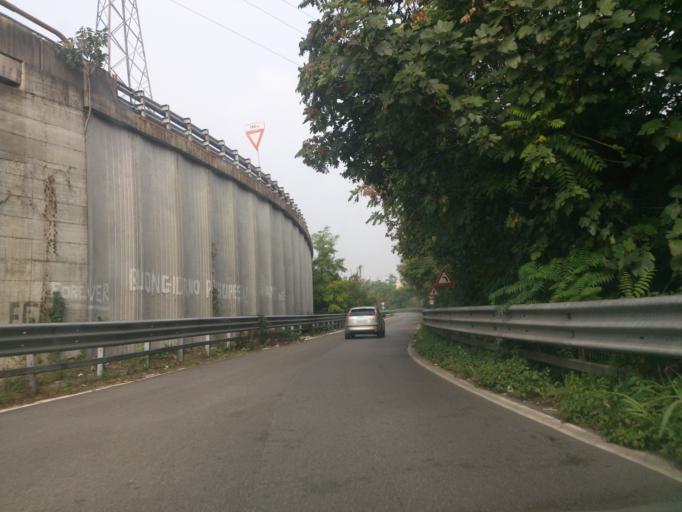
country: IT
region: Lombardy
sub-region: Citta metropolitana di Milano
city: Chiaravalle
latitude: 45.4251
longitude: 9.2490
